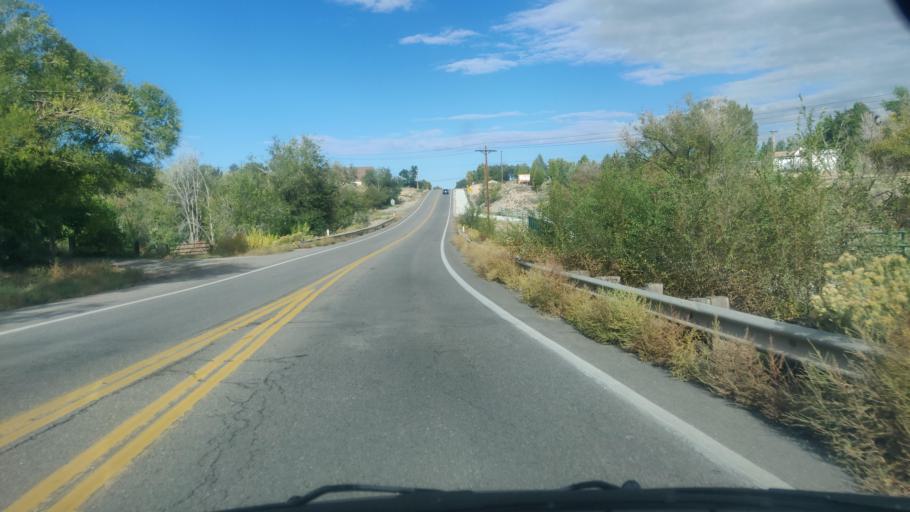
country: US
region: Colorado
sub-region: Mesa County
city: Redlands
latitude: 39.0699
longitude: -108.6159
